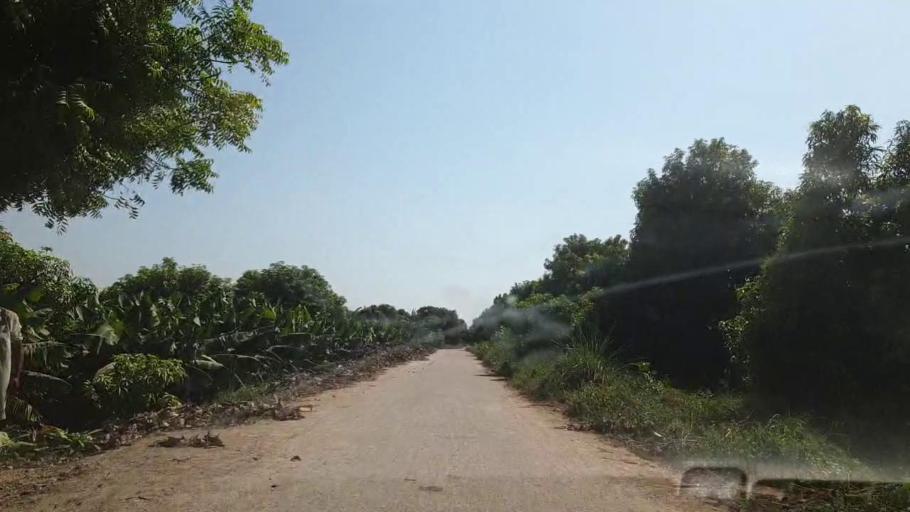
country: PK
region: Sindh
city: Tando Jam
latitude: 25.4106
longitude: 68.5821
